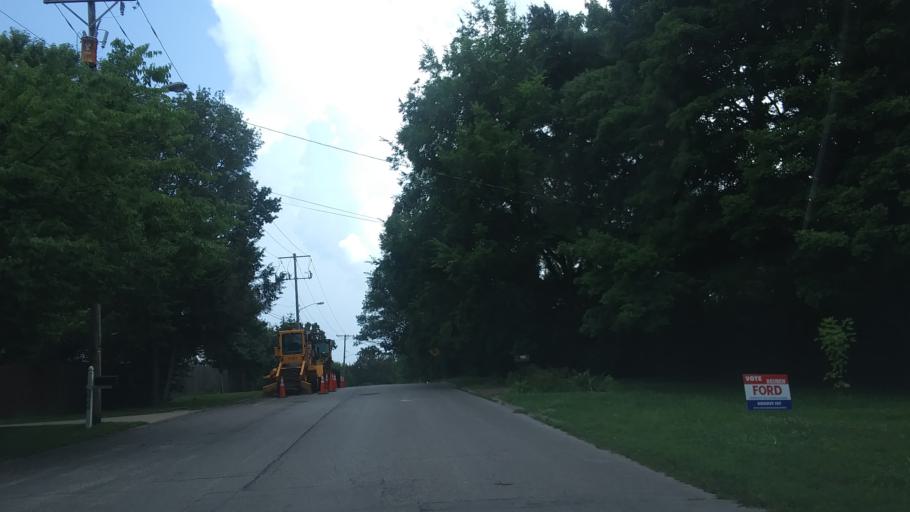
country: US
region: Tennessee
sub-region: Davidson County
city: Oak Hill
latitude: 36.0696
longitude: -86.7105
